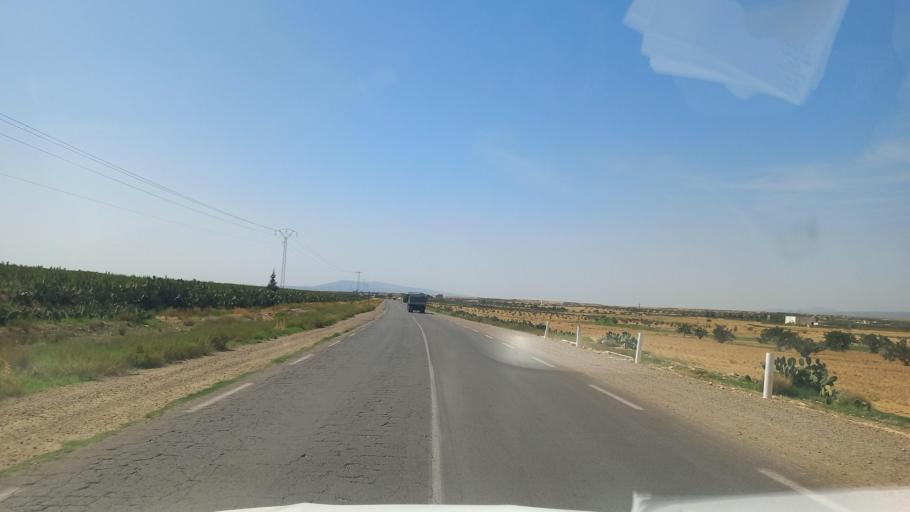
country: TN
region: Al Qasrayn
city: Sbiba
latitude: 35.3732
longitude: 9.0998
